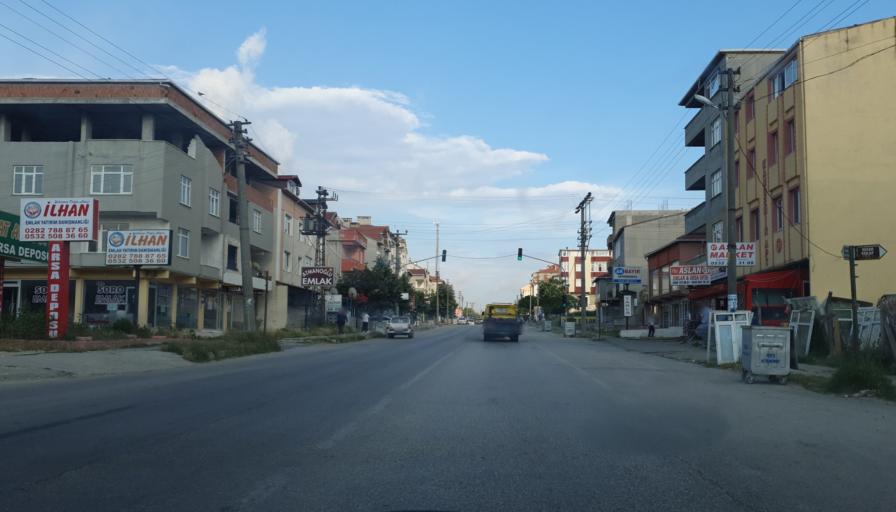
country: TR
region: Tekirdag
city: Saray
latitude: 41.3595
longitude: 27.9468
